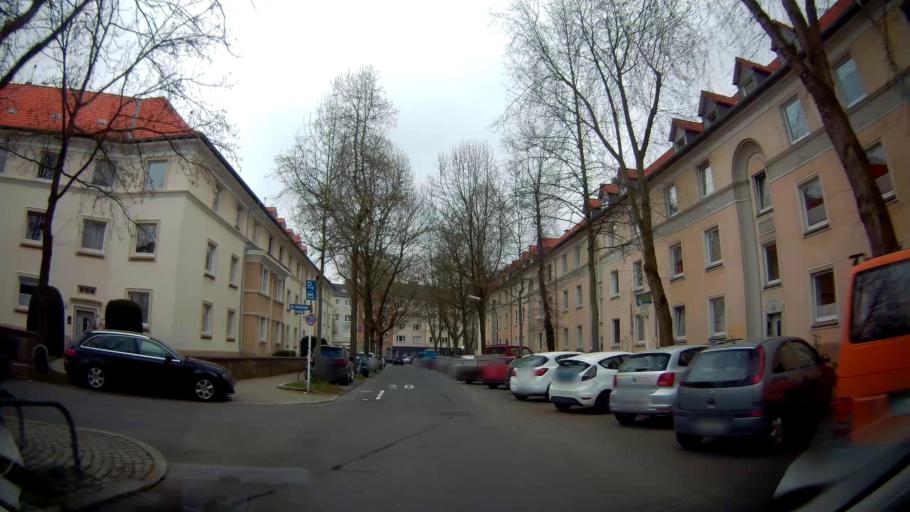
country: DE
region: North Rhine-Westphalia
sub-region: Regierungsbezirk Arnsberg
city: Dortmund
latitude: 51.5089
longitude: 7.4872
